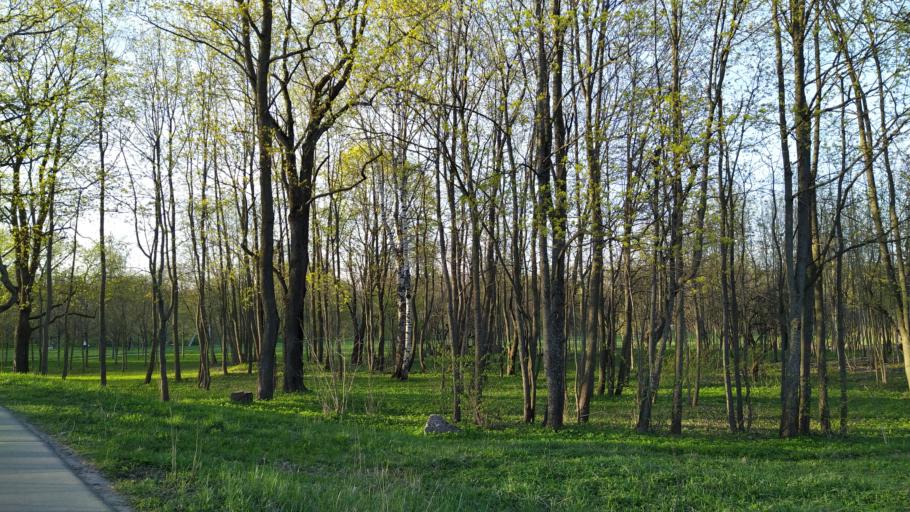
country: RU
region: St.-Petersburg
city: Pavlovsk
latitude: 59.7024
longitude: 30.4210
